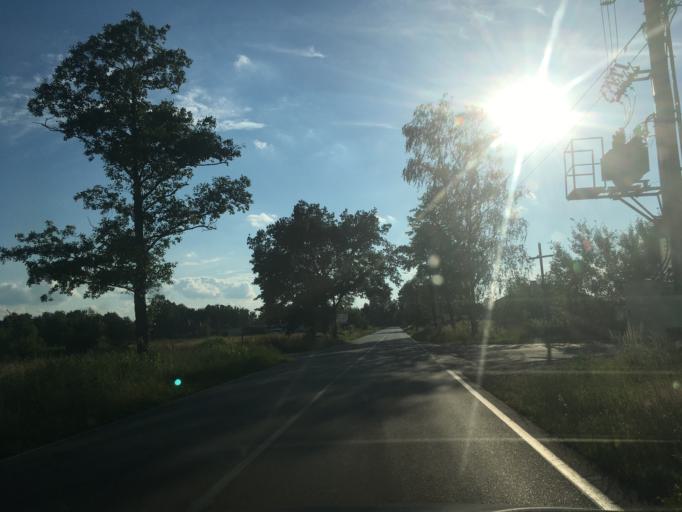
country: PL
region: Masovian Voivodeship
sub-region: Powiat wolominski
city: Radzymin
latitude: 52.4114
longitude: 21.2249
